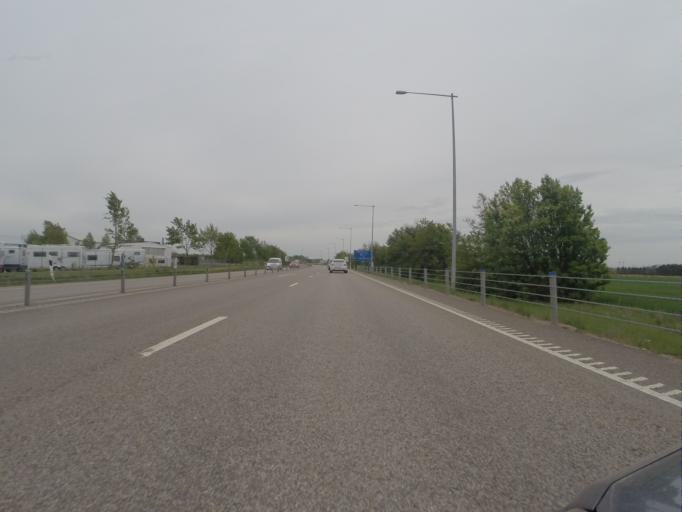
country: SE
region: Skane
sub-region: Helsingborg
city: Morarp
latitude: 56.0823
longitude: 12.8857
